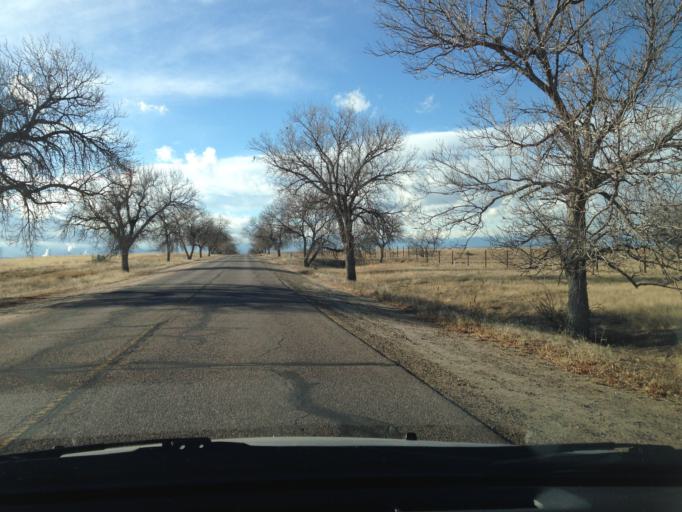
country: US
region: Colorado
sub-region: Adams County
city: Derby
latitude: 39.8273
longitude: -104.8680
